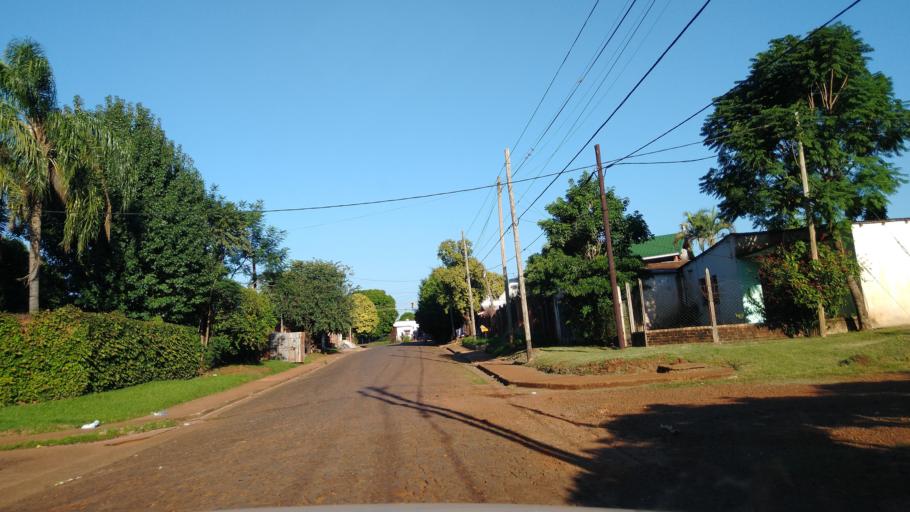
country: AR
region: Misiones
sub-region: Departamento de Capital
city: Posadas
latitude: -27.4067
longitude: -55.9253
